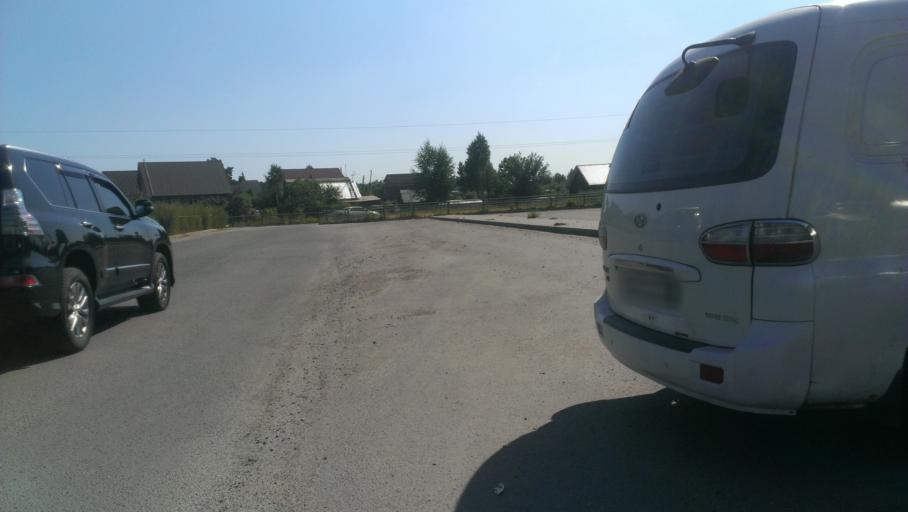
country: RU
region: Altai Krai
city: Novosilikatnyy
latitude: 53.3251
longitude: 83.6828
